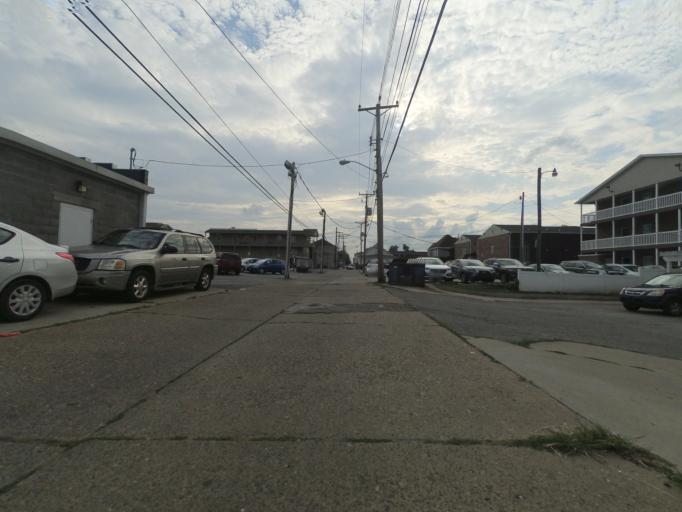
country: US
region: West Virginia
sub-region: Cabell County
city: Huntington
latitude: 38.4197
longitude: -82.4296
